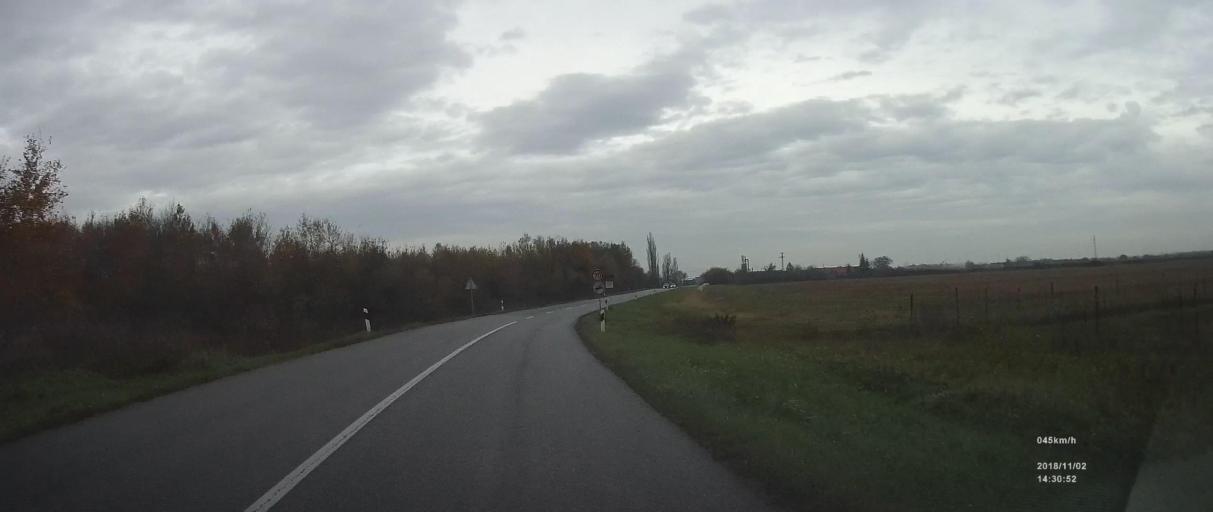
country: HR
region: Zagrebacka
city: Gradici
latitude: 45.6811
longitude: 16.0559
